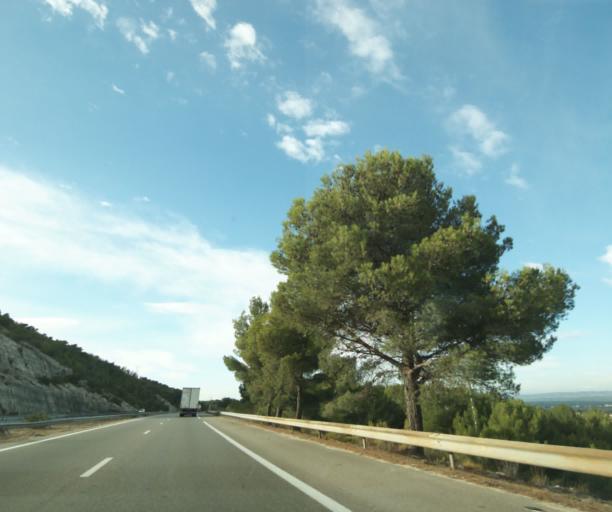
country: FR
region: Provence-Alpes-Cote d'Azur
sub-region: Departement des Bouches-du-Rhone
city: Chateauneuf-les-Martigues
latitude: 43.3808
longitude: 5.1596
